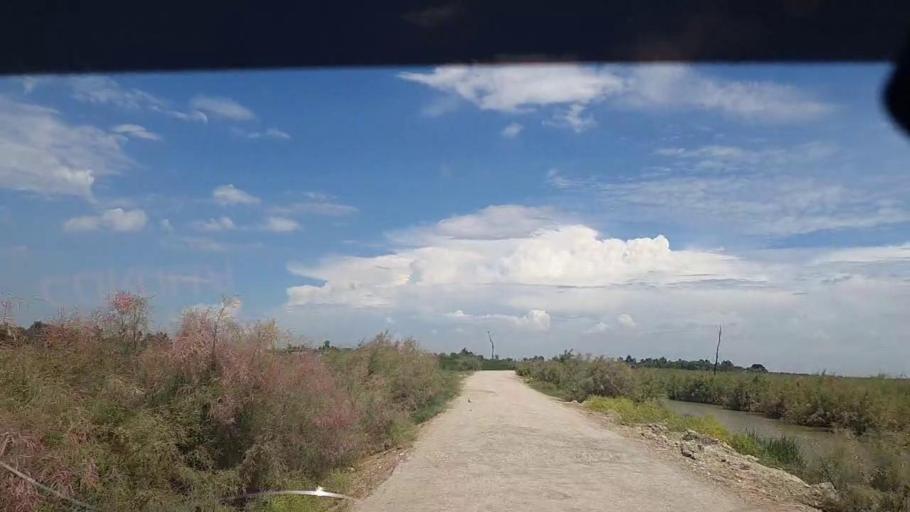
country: PK
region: Sindh
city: Ghauspur
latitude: 28.1492
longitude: 68.9854
